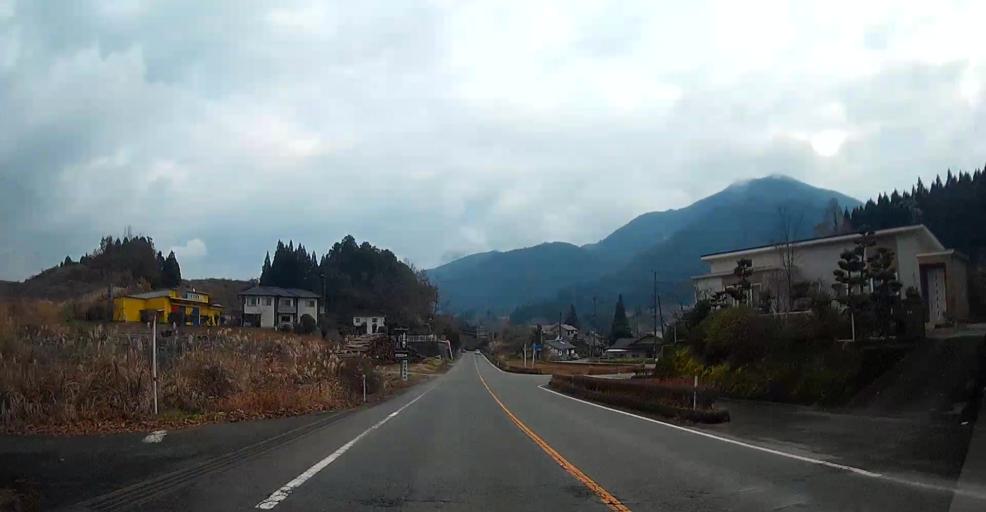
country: JP
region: Kumamoto
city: Matsubase
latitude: 32.6241
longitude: 130.8782
